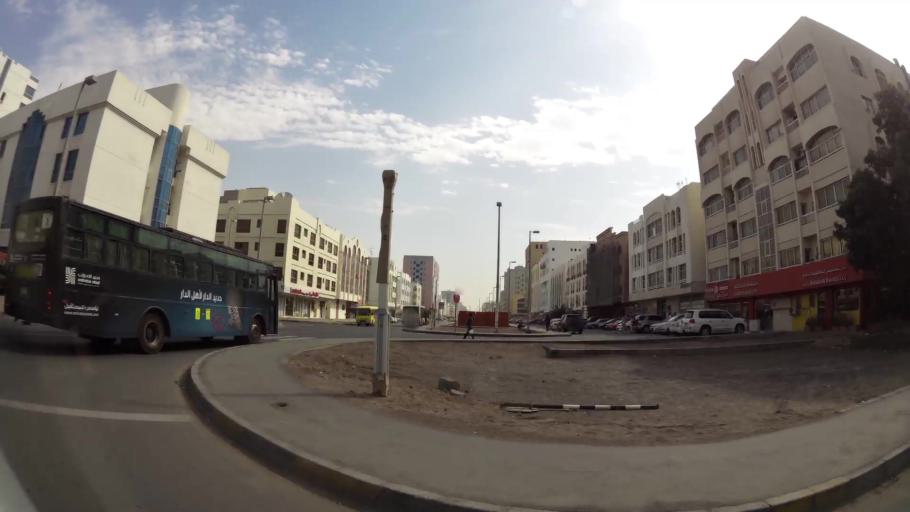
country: AE
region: Abu Dhabi
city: Abu Dhabi
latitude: 24.3357
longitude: 54.5347
